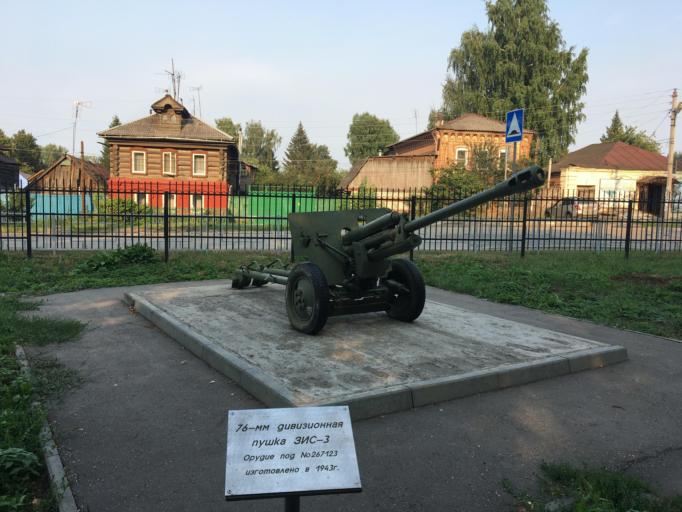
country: RU
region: Nizjnij Novgorod
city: Lyskovo
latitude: 56.0398
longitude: 45.0462
